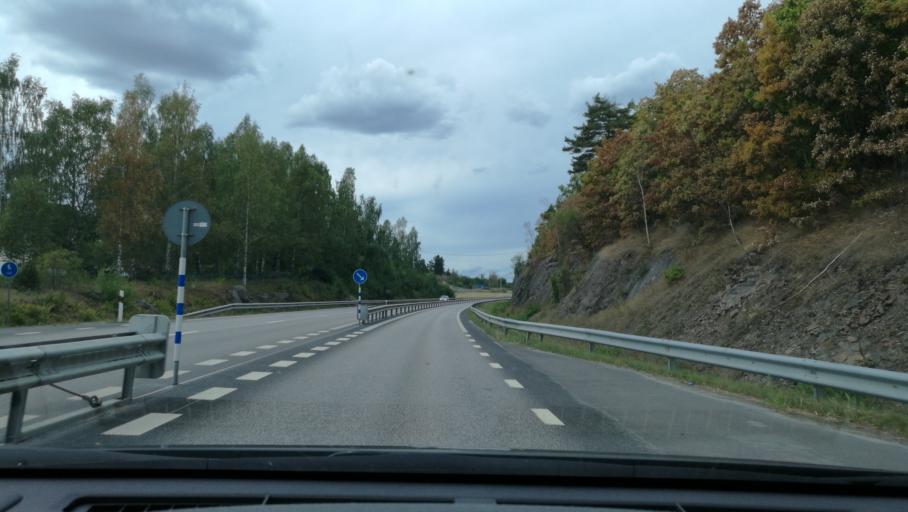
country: SE
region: OEstergoetland
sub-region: Norrkopings Kommun
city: Svartinge
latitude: 58.6811
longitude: 15.9419
